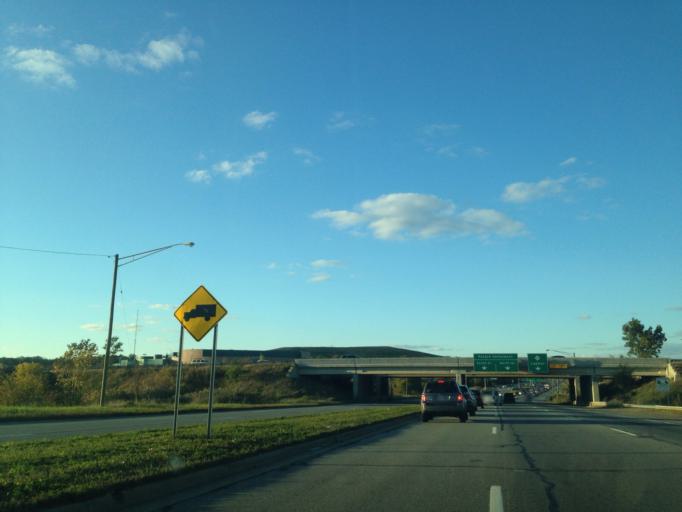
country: US
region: Michigan
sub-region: Oakland County
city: Auburn Hills
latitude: 42.6921
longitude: -83.2415
